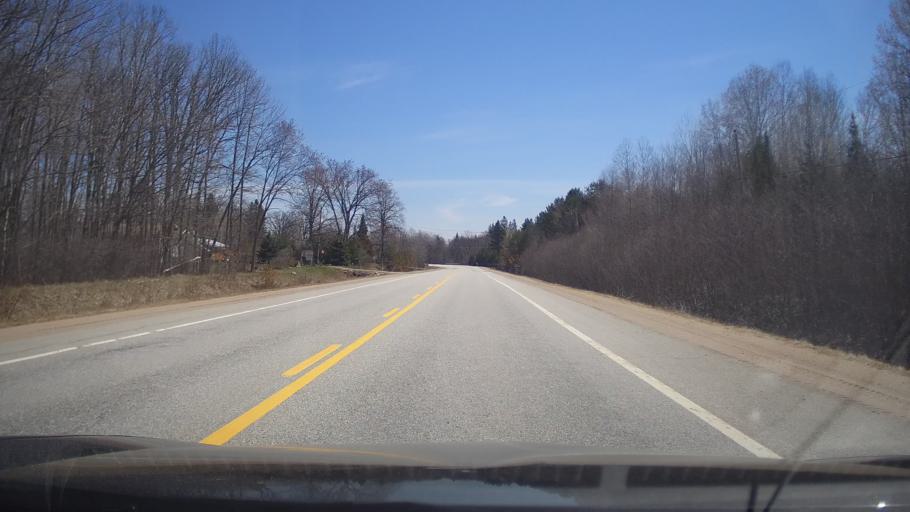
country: CA
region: Ontario
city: Arnprior
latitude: 45.5283
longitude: -76.1975
